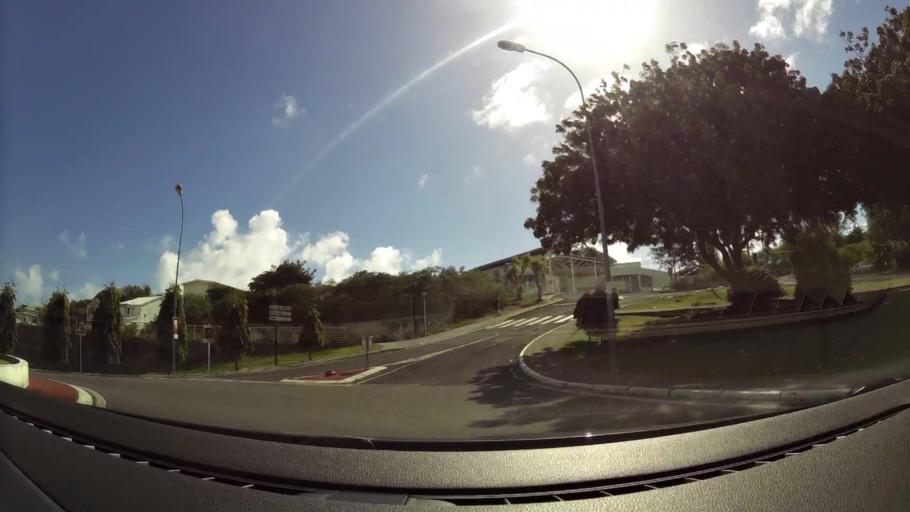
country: GP
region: Guadeloupe
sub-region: Guadeloupe
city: Saint-Francois
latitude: 16.2517
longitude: -61.2877
